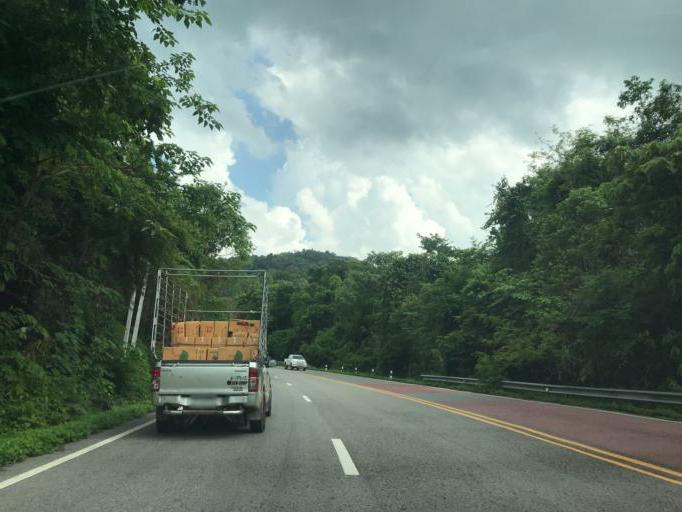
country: TH
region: Phayao
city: Phayao
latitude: 19.0671
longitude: 99.8025
